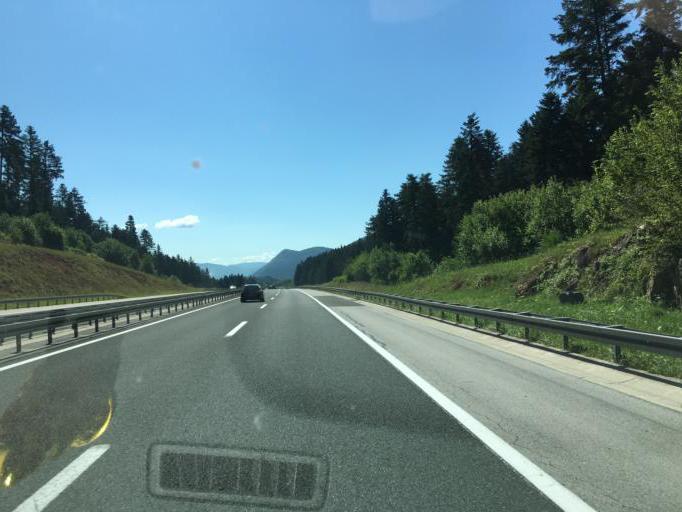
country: HR
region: Licko-Senjska
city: Otocac
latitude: 44.8492
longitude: 15.2322
